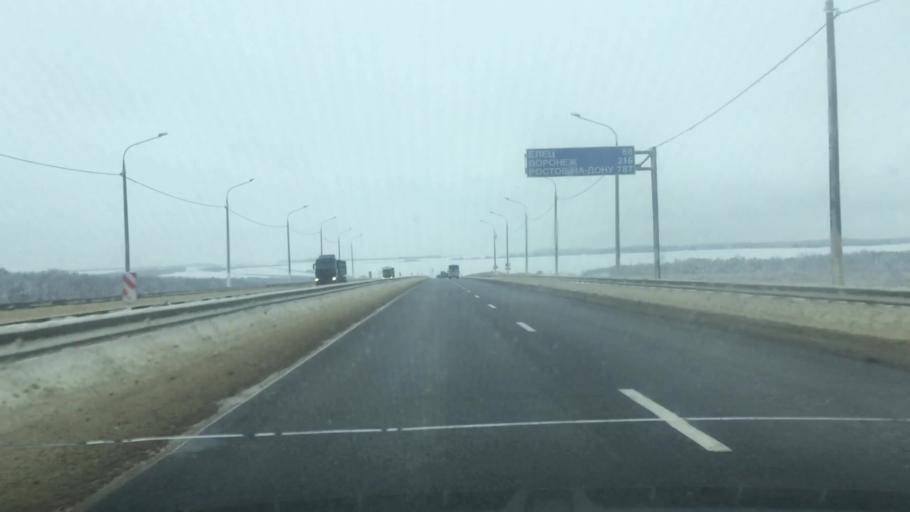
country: RU
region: Tula
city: Kazachka
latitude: 53.2878
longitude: 38.1788
